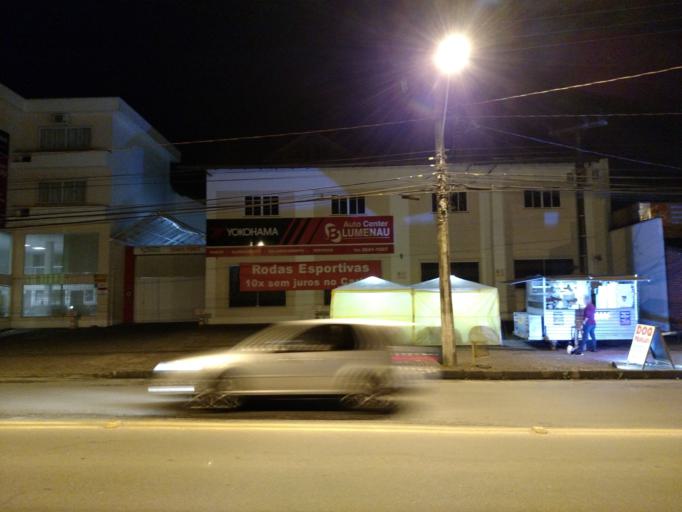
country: BR
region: Santa Catarina
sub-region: Blumenau
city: Blumenau
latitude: -26.9137
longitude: -49.0830
